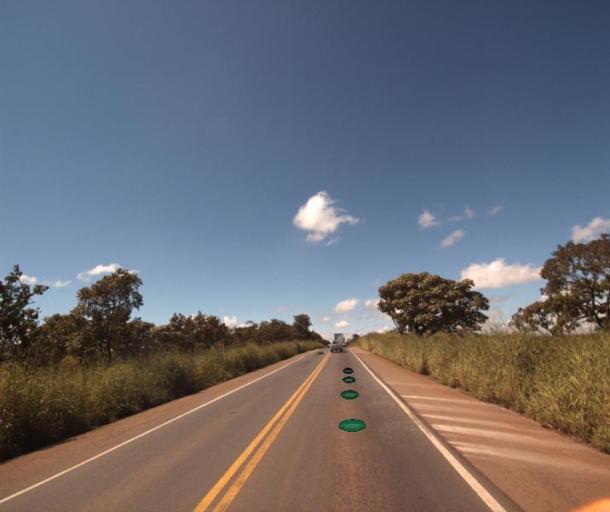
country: BR
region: Goias
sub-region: Jaragua
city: Jaragua
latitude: -15.6401
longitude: -49.3722
